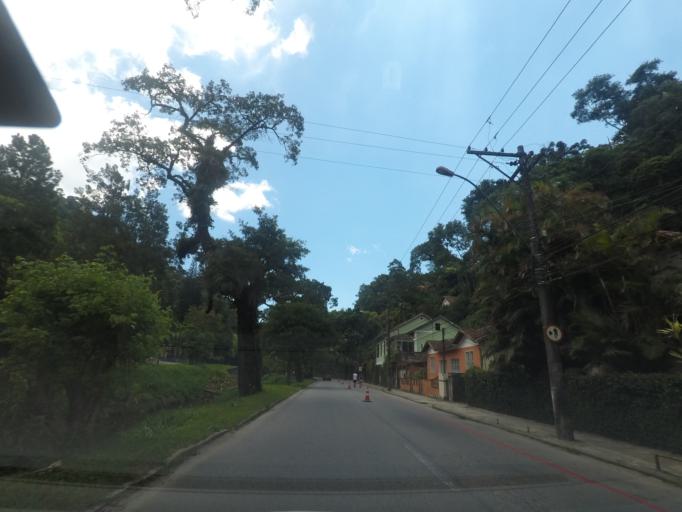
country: BR
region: Rio de Janeiro
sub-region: Petropolis
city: Petropolis
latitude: -22.5026
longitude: -43.1817
